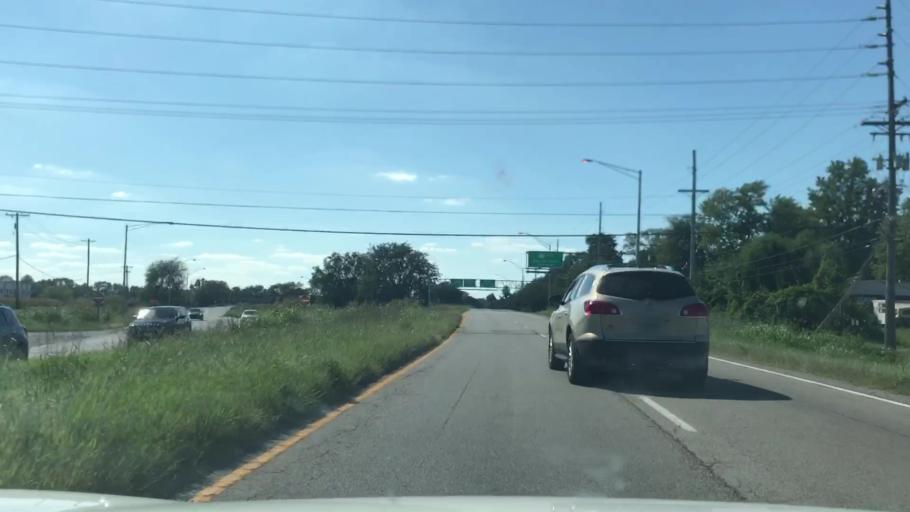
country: US
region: Illinois
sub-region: Saint Clair County
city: Swansea
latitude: 38.5476
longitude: -90.0570
